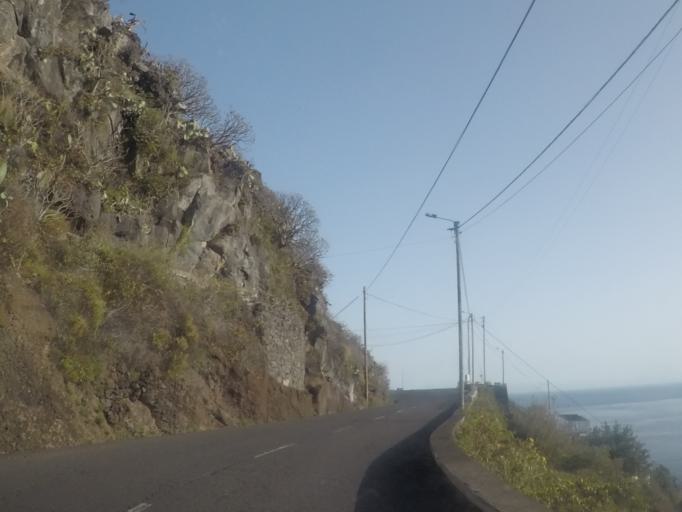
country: PT
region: Madeira
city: Ribeira Brava
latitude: 32.6782
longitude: -17.0714
